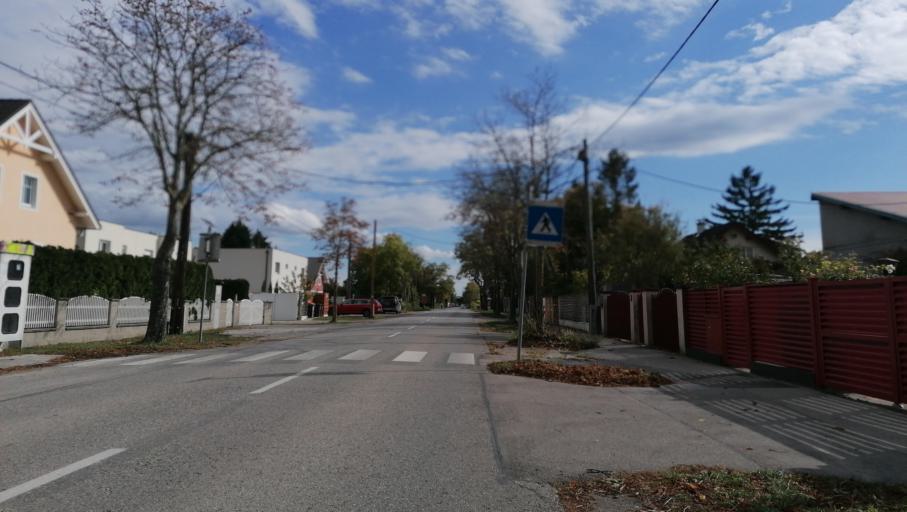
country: AT
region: Lower Austria
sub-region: Politischer Bezirk Baden
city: Teesdorf
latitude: 47.9791
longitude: 16.2760
